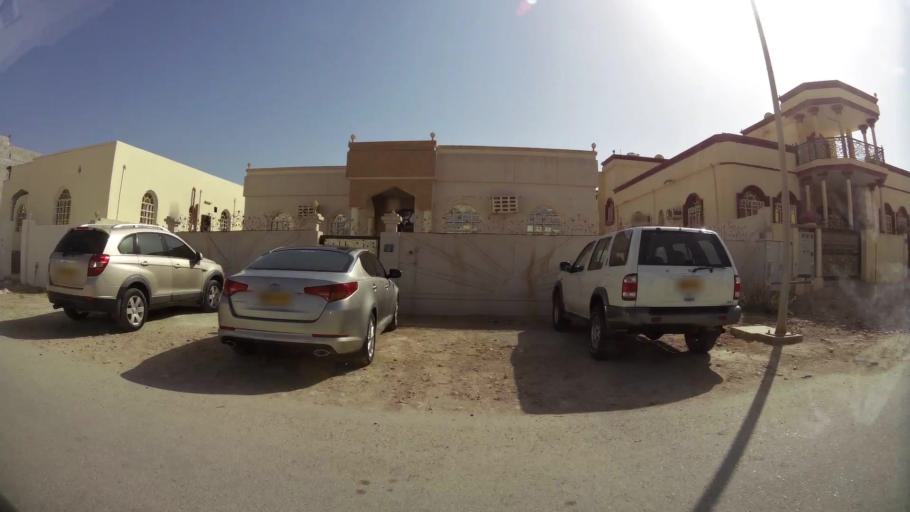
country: OM
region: Zufar
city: Salalah
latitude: 17.0055
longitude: 54.0050
